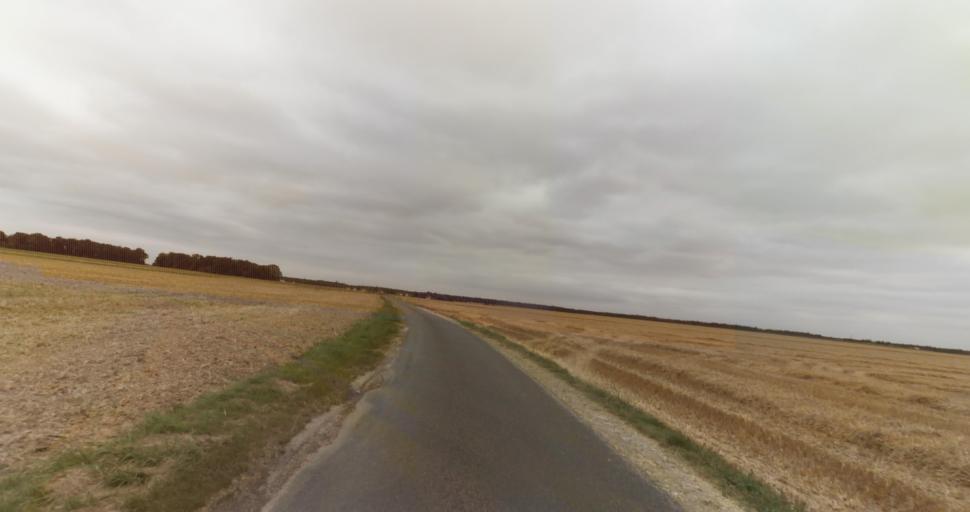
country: FR
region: Haute-Normandie
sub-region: Departement de l'Eure
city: La Couture-Boussey
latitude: 48.9231
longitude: 1.3939
